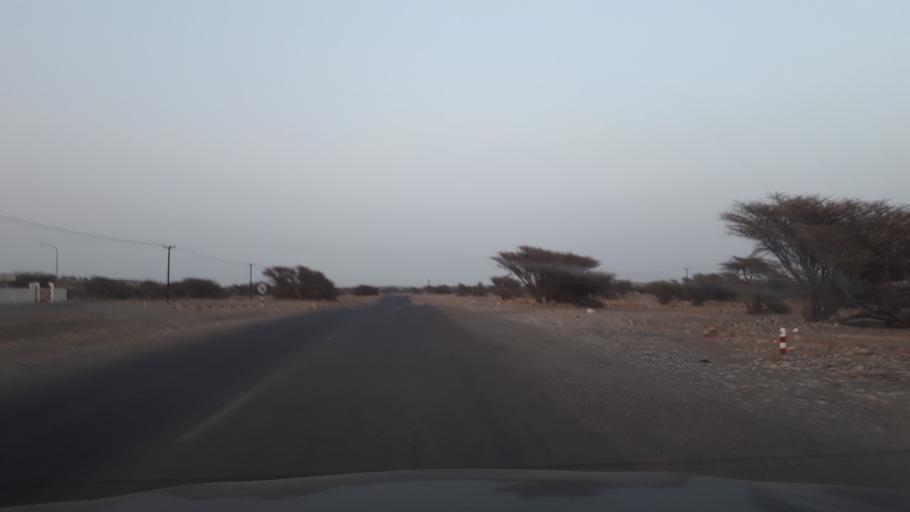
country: OM
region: Al Batinah
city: Rustaq
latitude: 23.5513
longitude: 57.5450
